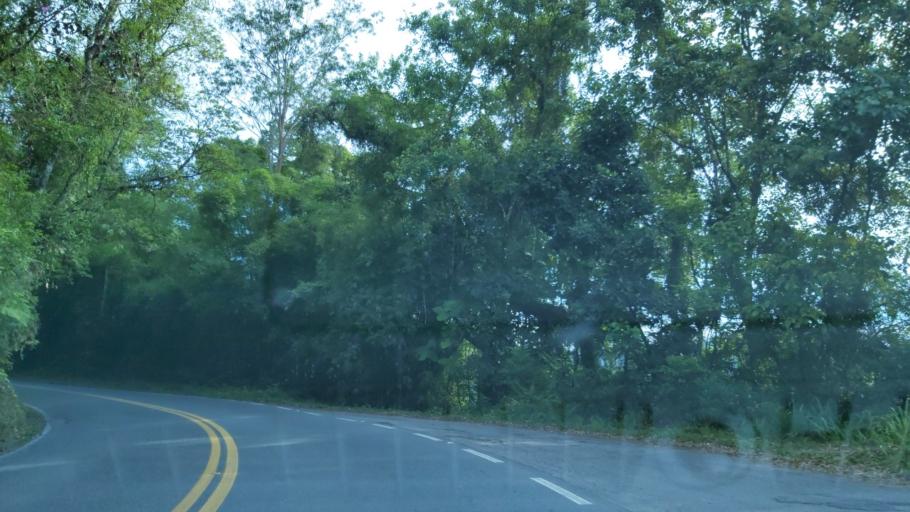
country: BR
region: Sao Paulo
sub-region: Juquia
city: Juquia
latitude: -24.1078
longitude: -47.6245
